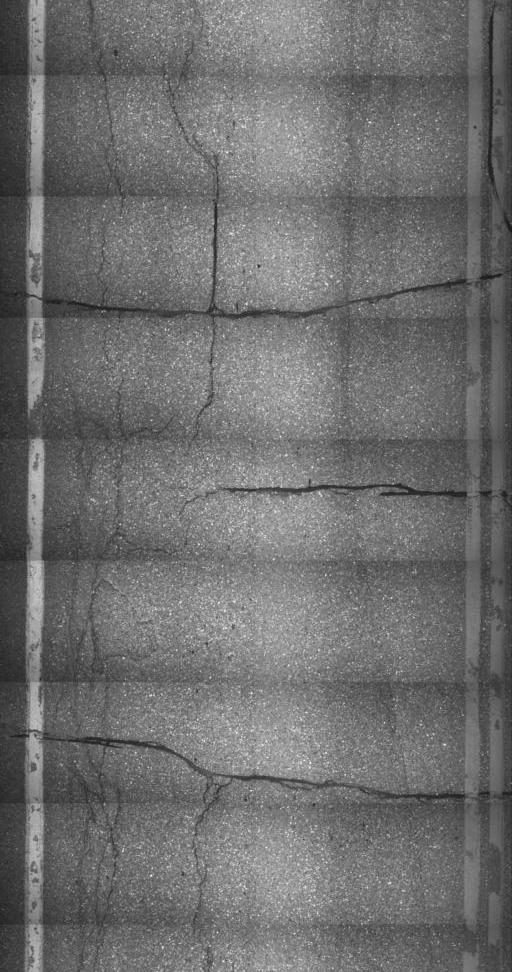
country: US
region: Vermont
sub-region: Franklin County
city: Saint Albans
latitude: 44.7387
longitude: -73.1152
